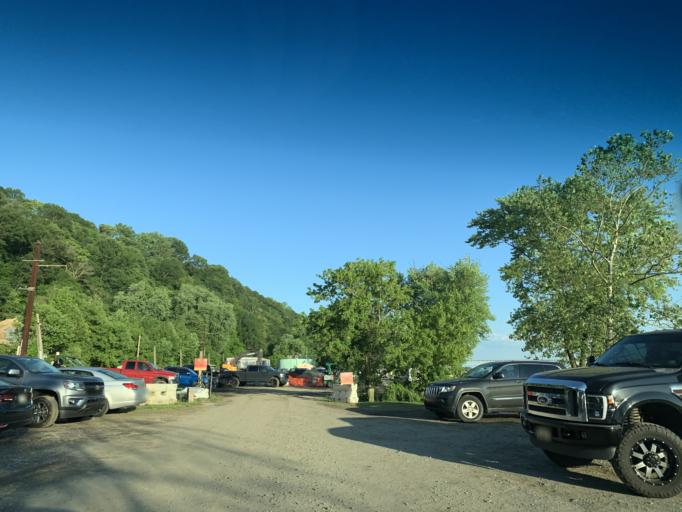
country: US
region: Maryland
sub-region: Harford County
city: Havre de Grace
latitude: 39.5990
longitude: -76.1099
